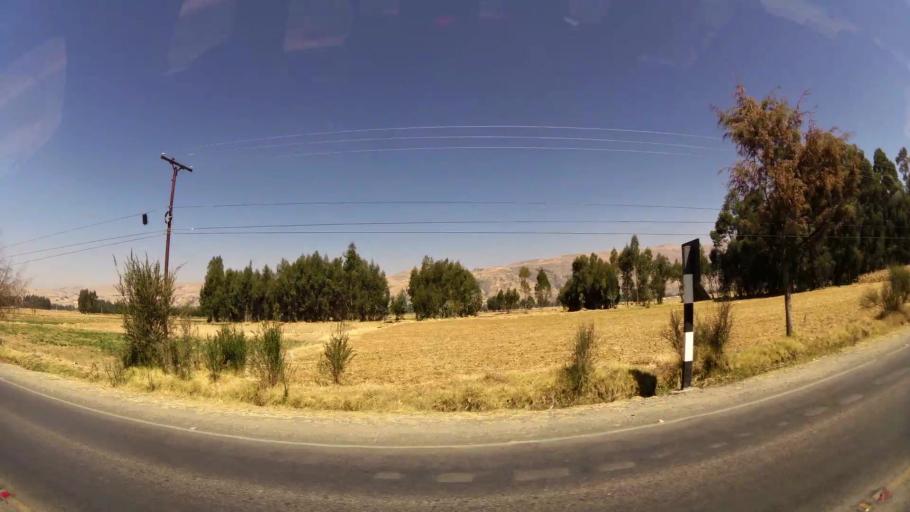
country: PE
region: Junin
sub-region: Provincia de Jauja
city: San Lorenzo
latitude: -11.8585
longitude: -75.3771
